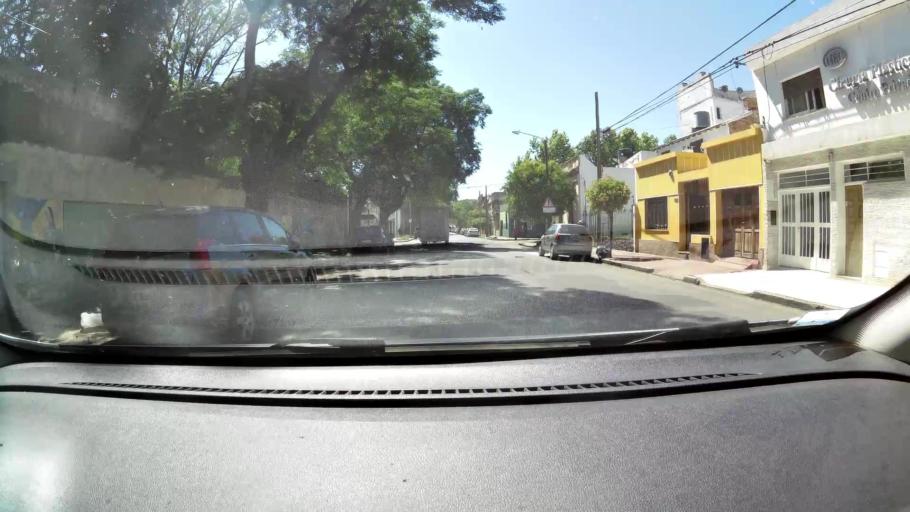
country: AR
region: Cordoba
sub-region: Departamento de Capital
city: Cordoba
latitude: -31.4225
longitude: -64.1456
